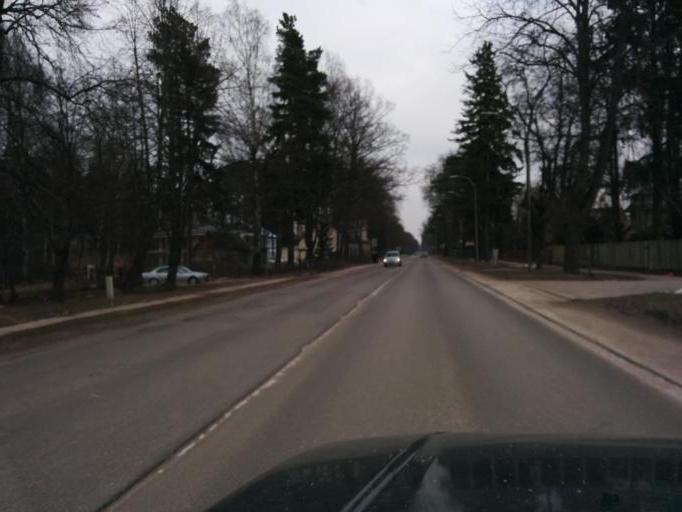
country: LV
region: Jurmala
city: Jurmala
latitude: 56.9596
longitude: 23.6970
